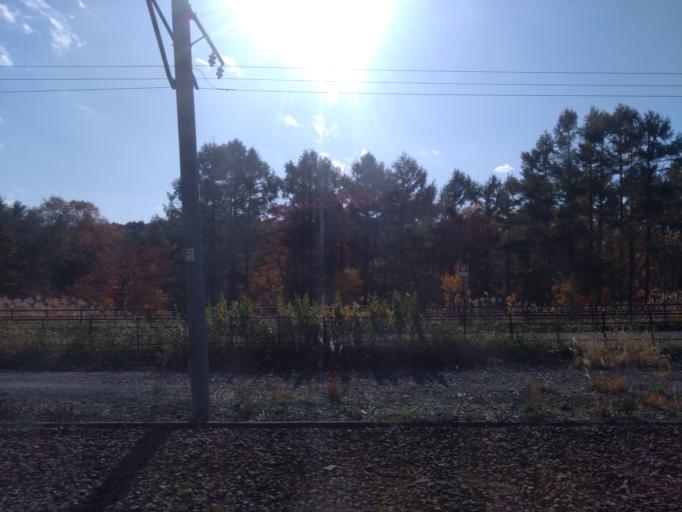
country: JP
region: Hokkaido
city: Kitahiroshima
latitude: 42.9982
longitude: 141.5305
